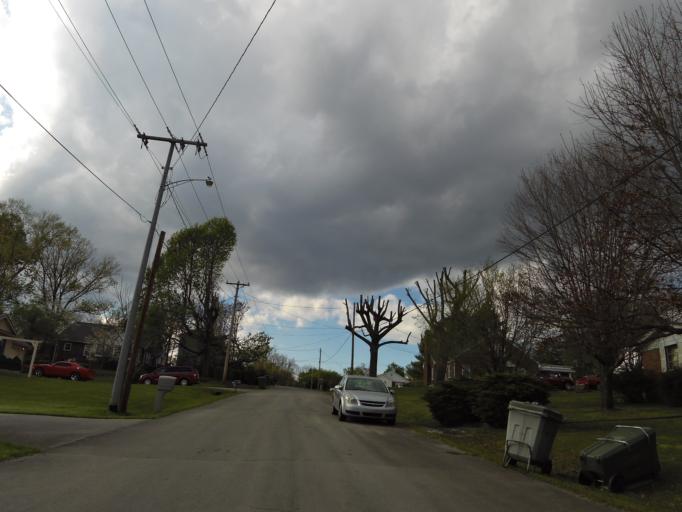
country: US
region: Tennessee
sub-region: Blount County
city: Maryville
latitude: 35.7607
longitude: -83.9618
